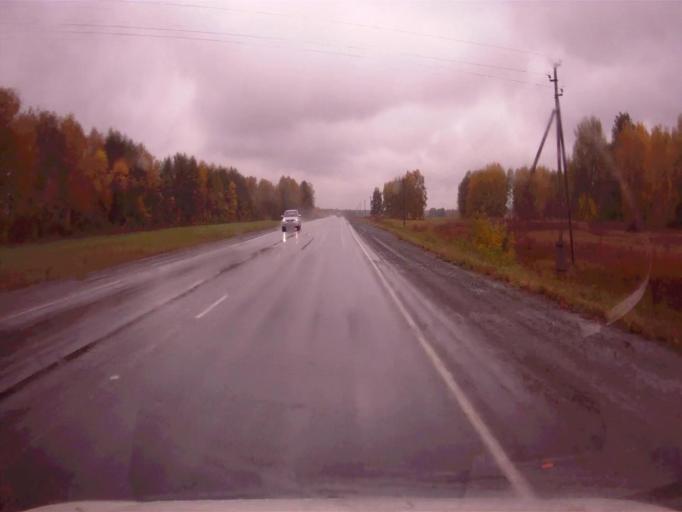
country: RU
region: Chelyabinsk
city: Roshchino
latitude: 55.4011
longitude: 61.0718
